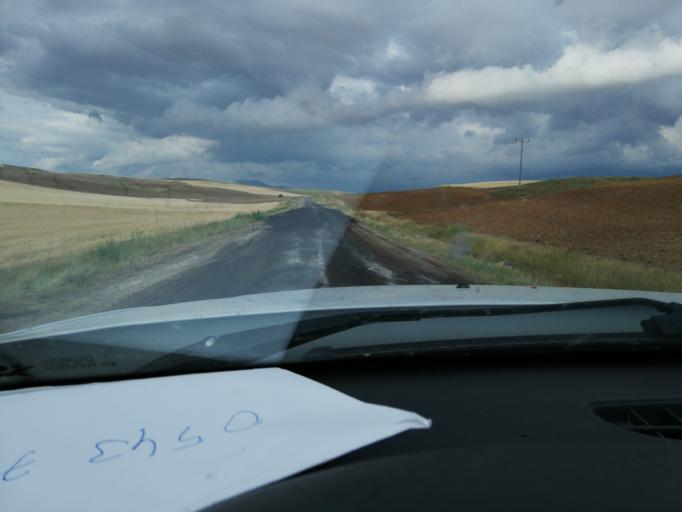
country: TR
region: Kirsehir
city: Kirsehir
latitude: 39.0405
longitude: 34.1516
